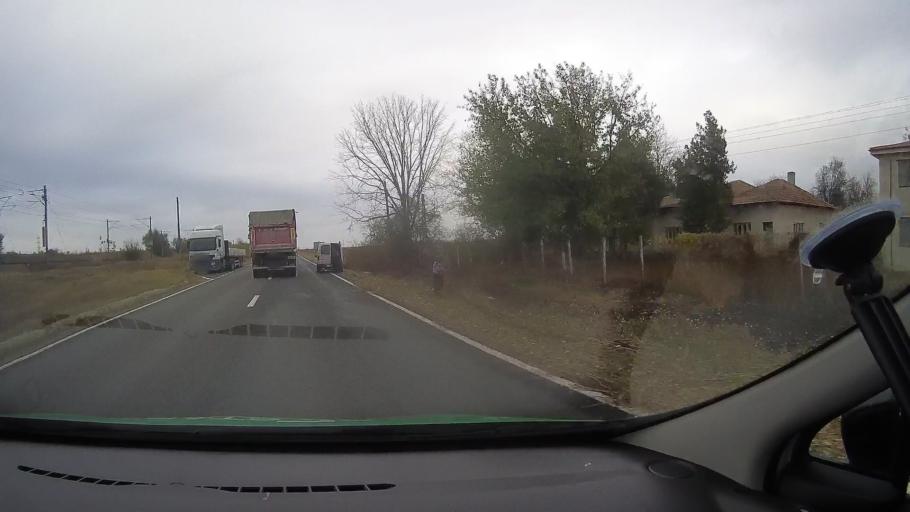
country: RO
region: Constanta
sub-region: Comuna Poarta Alba
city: Poarta Alba
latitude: 44.2268
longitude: 28.3819
